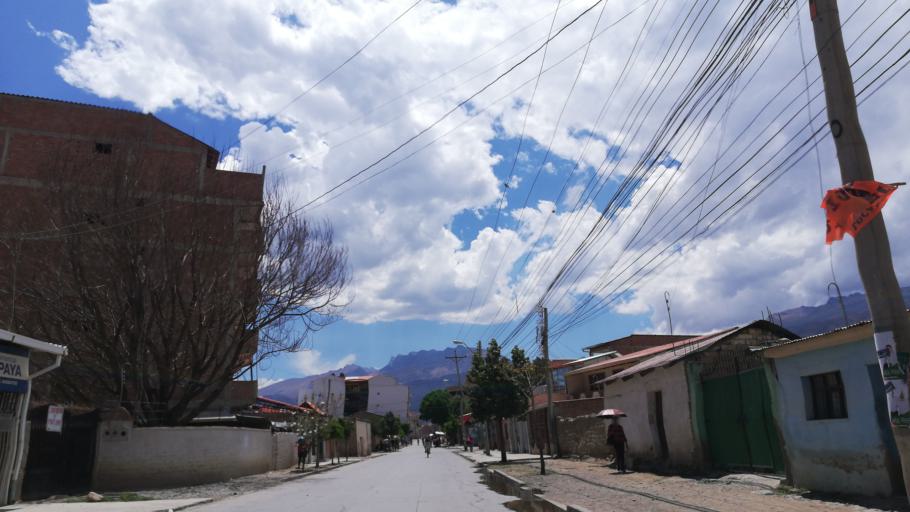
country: BO
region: Cochabamba
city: Cochabamba
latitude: -17.3408
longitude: -66.2148
